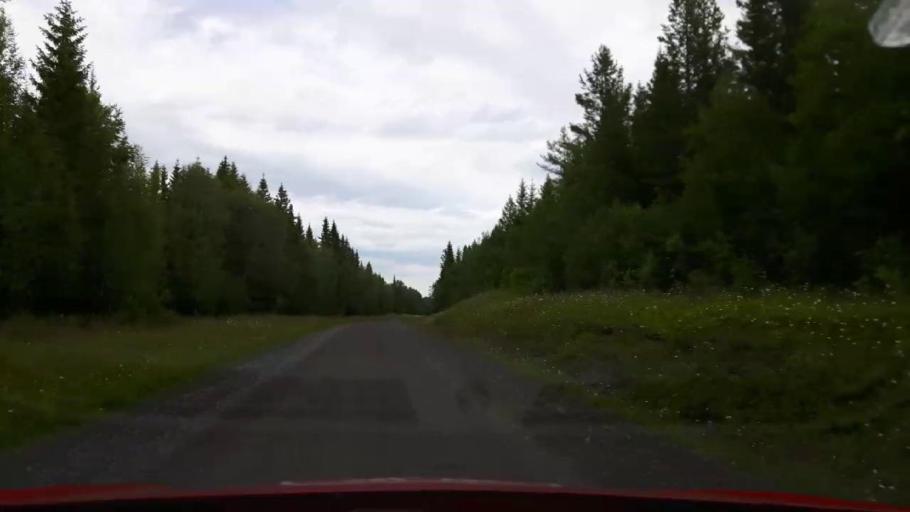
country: SE
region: Jaemtland
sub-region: OEstersunds Kommun
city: Lit
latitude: 63.4026
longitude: 15.2325
